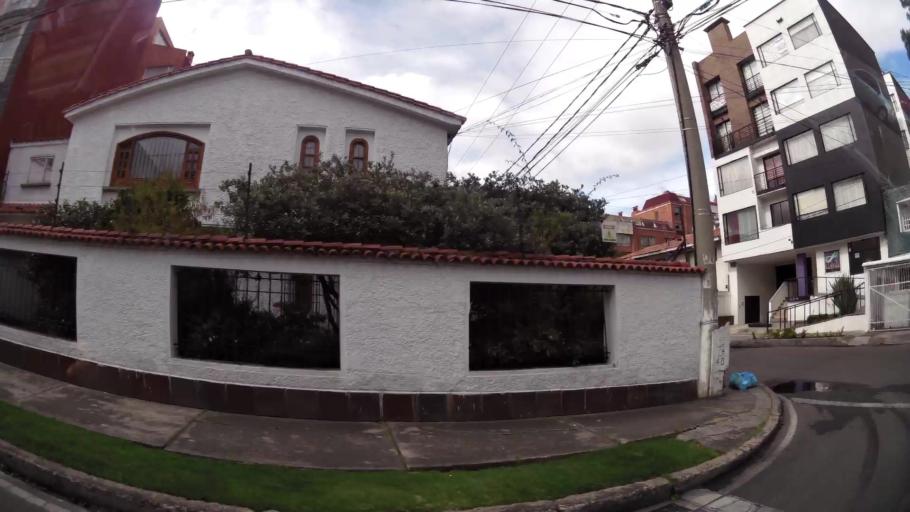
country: CO
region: Bogota D.C.
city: Barrio San Luis
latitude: 4.6960
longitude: -74.0635
